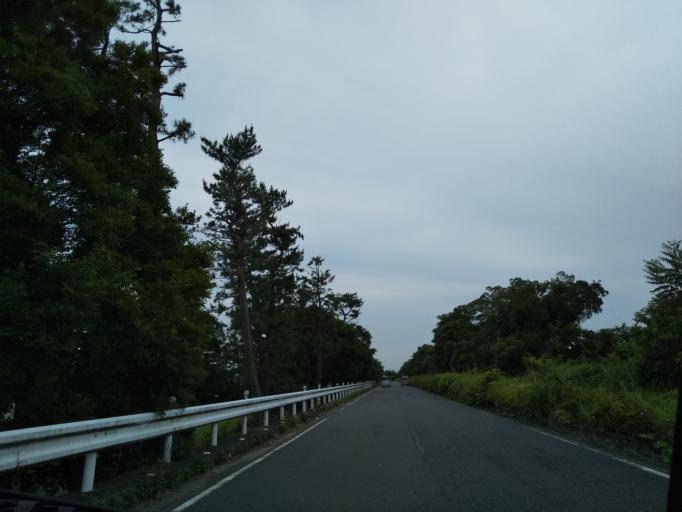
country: JP
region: Kanagawa
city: Zama
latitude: 35.4953
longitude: 139.3492
